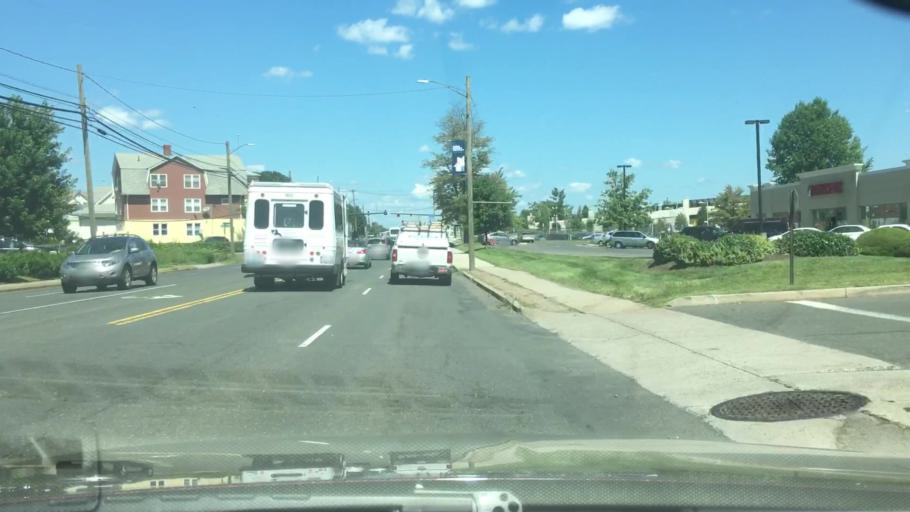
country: US
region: Connecticut
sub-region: Hartford County
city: West Hartford
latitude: 41.7406
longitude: -72.7182
